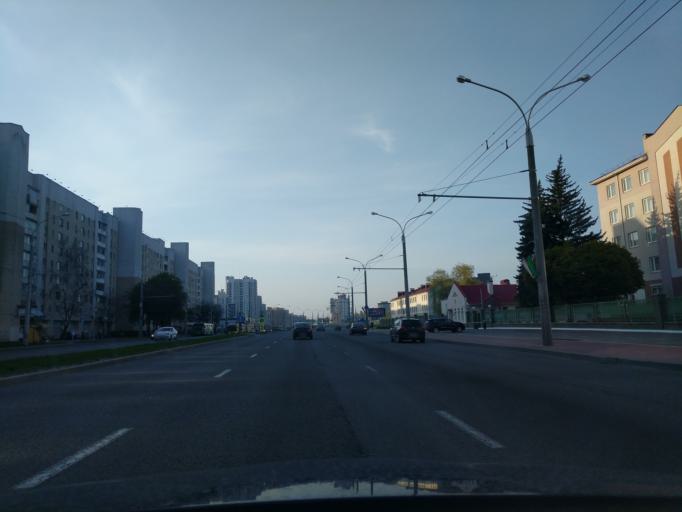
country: BY
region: Minsk
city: Minsk
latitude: 53.8676
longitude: 27.5705
